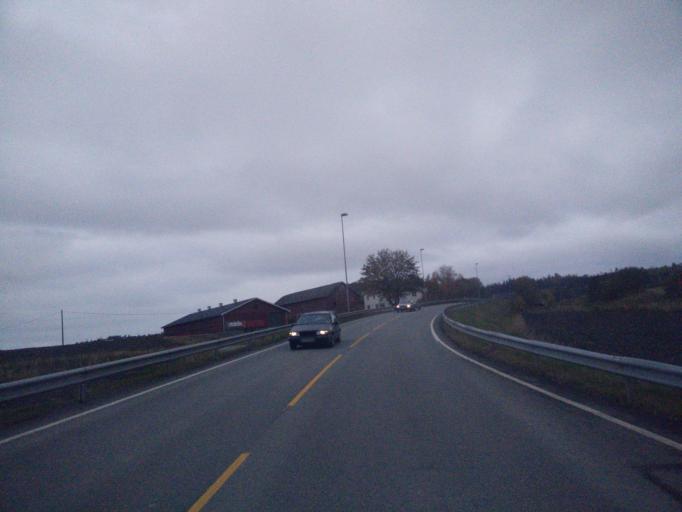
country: NO
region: Nord-Trondelag
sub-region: Stjordal
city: Stjordal
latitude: 63.5029
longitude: 10.8599
